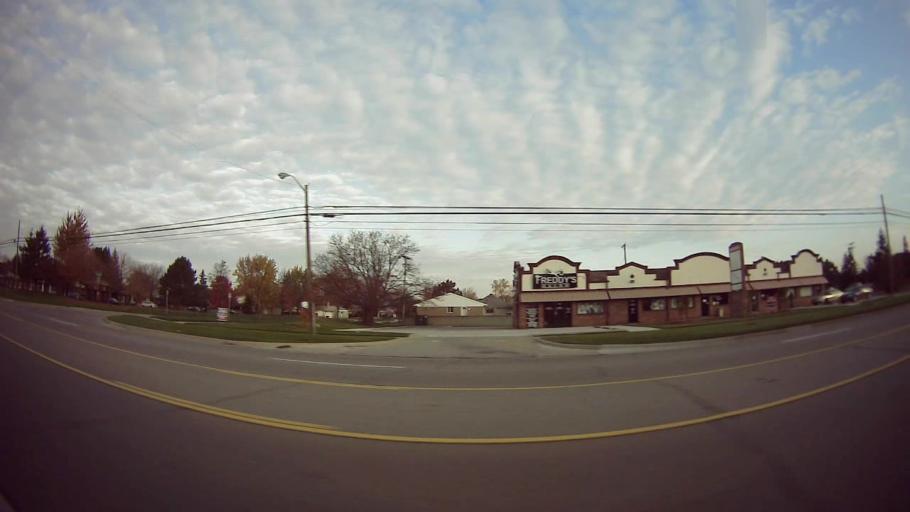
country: US
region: Michigan
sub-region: Macomb County
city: Sterling Heights
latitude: 42.5516
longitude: -83.0140
